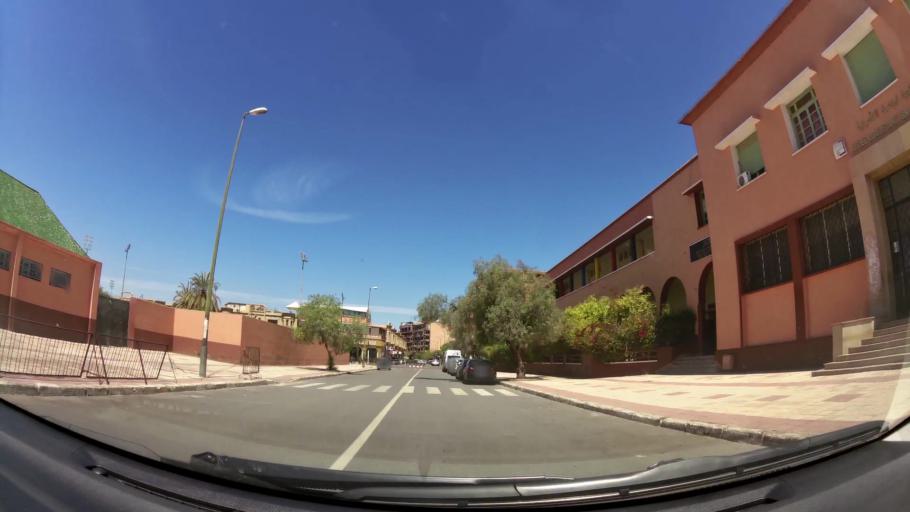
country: MA
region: Marrakech-Tensift-Al Haouz
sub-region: Marrakech
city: Marrakesh
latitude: 31.6269
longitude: -8.0064
